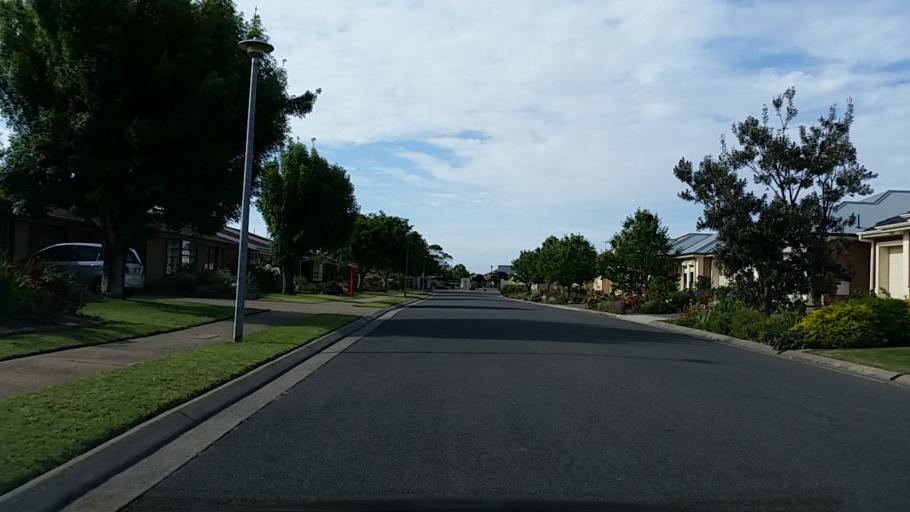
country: AU
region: South Australia
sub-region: Charles Sturt
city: Grange
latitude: -34.8966
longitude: 138.4995
